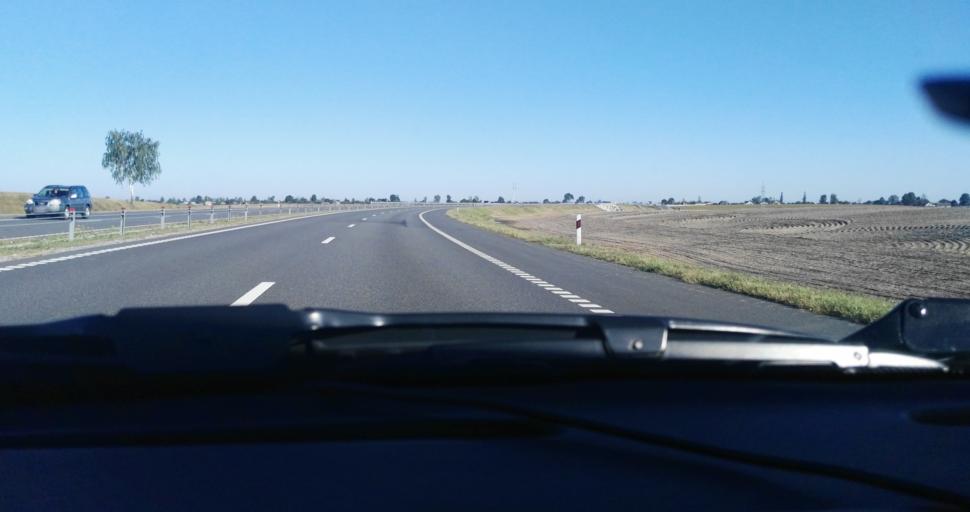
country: BY
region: Gomel
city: Buda-Kashalyova
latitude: 52.5093
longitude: 30.6326
